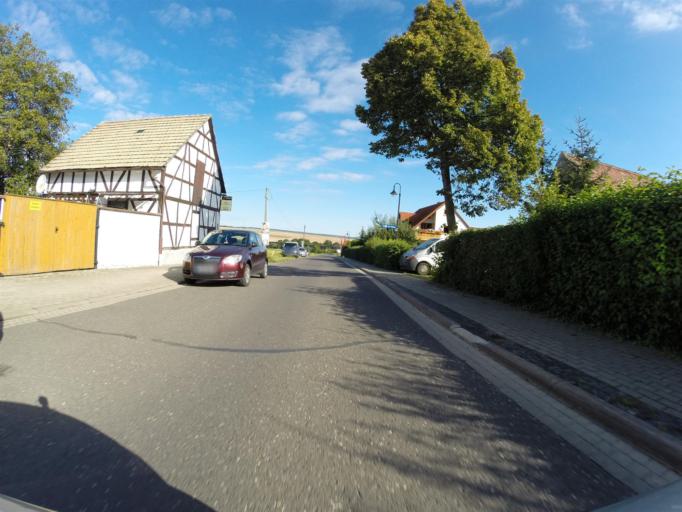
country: DE
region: Thuringia
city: Vollersroda
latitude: 50.9382
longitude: 11.3313
